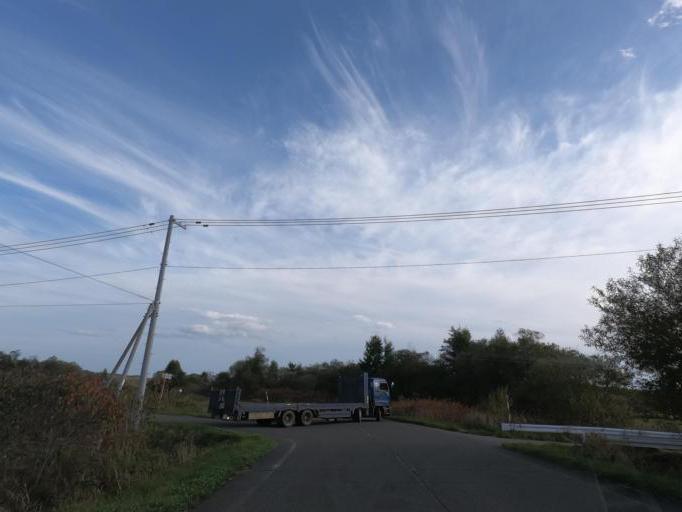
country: JP
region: Hokkaido
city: Obihiro
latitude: 42.5399
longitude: 143.3657
